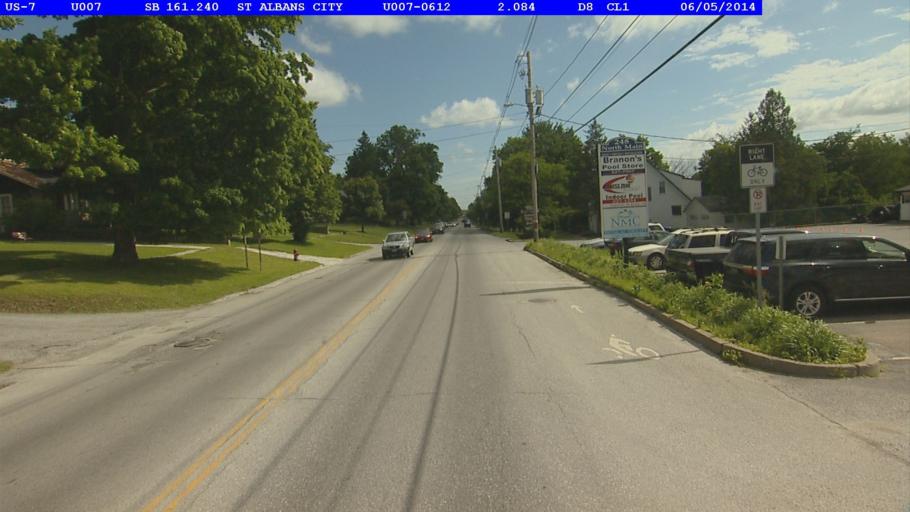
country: US
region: Vermont
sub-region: Franklin County
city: Saint Albans
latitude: 44.8227
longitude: -73.0812
